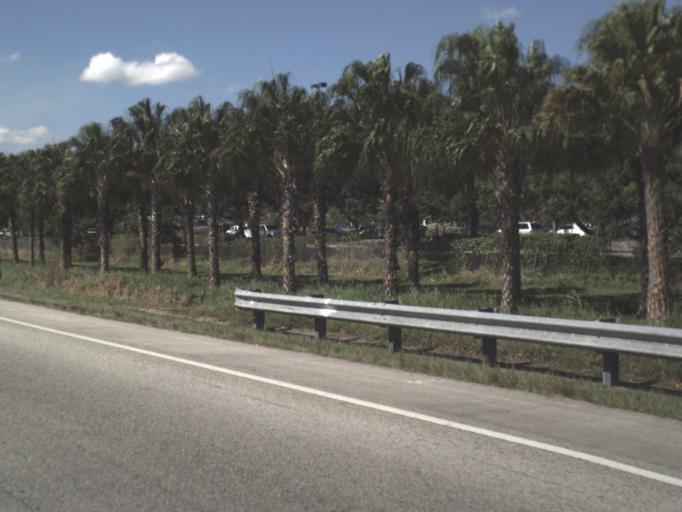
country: US
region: Florida
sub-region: Miami-Dade County
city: Florida City
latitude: 25.4562
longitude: -80.4717
